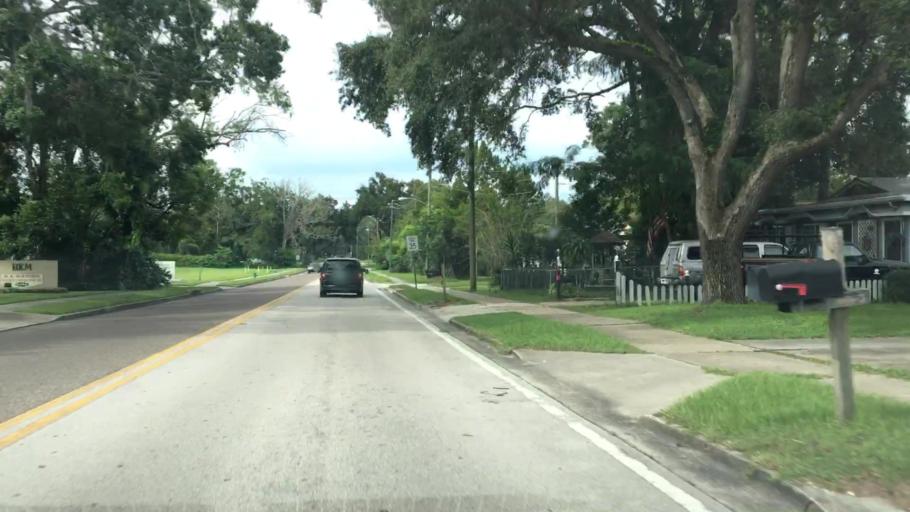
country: US
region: Florida
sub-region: Seminole County
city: Sanford
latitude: 28.7878
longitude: -81.2648
